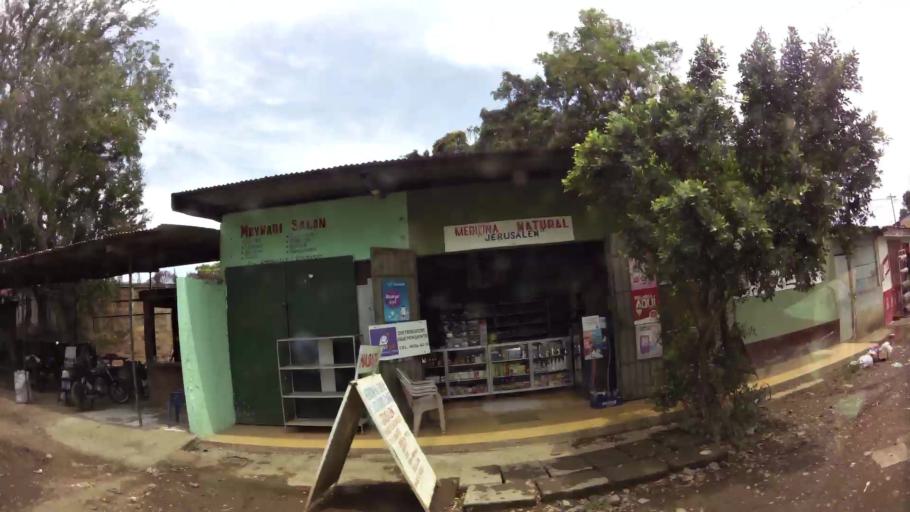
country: NI
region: Rivas
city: Rivas
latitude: 11.4399
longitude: -85.8333
